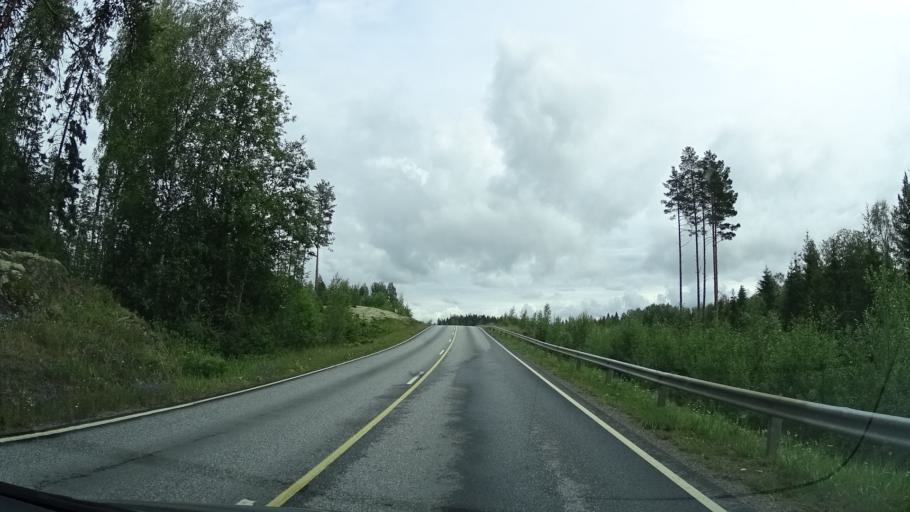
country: FI
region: Haeme
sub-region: Forssa
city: Humppila
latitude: 61.0970
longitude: 23.3477
